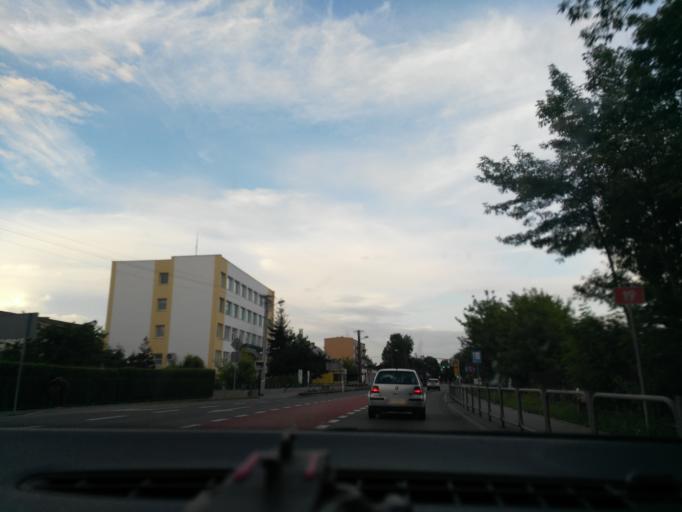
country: PL
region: Lublin Voivodeship
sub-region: Powiat lubelski
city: Niemce
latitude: 51.3584
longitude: 22.6227
